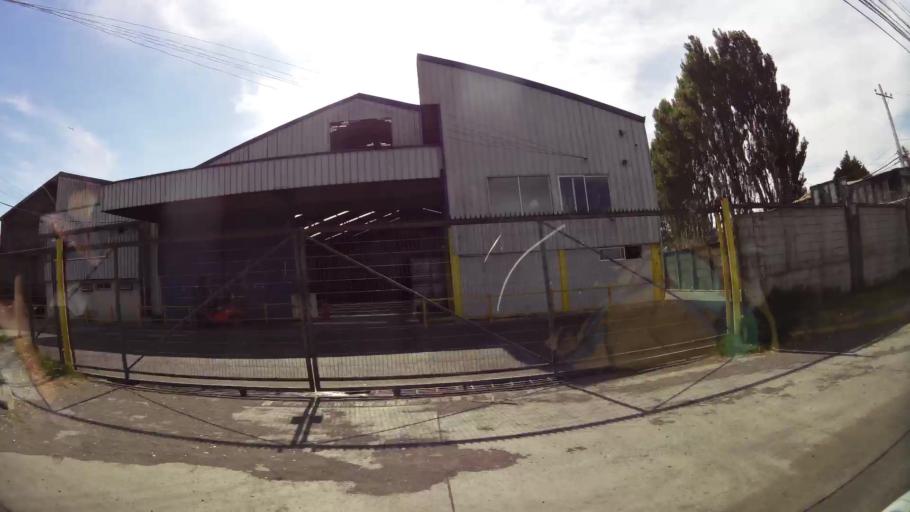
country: CL
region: Biobio
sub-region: Provincia de Concepcion
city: Talcahuano
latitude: -36.7694
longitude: -73.1149
